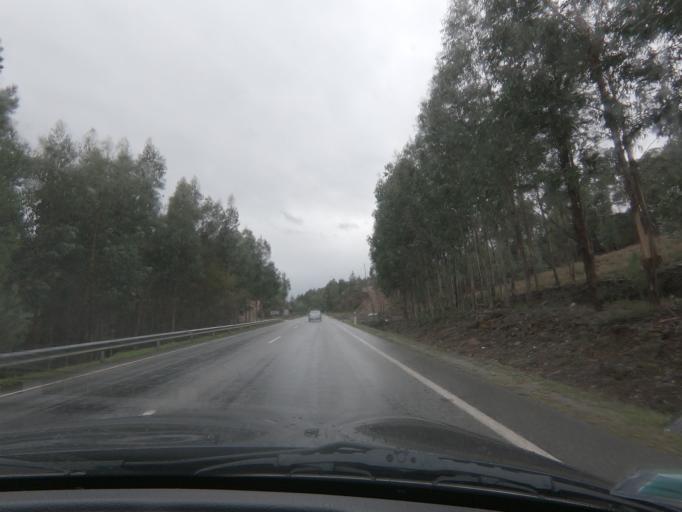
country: PT
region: Porto
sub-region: Amarante
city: Amarante
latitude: 41.3248
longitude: -8.0445
